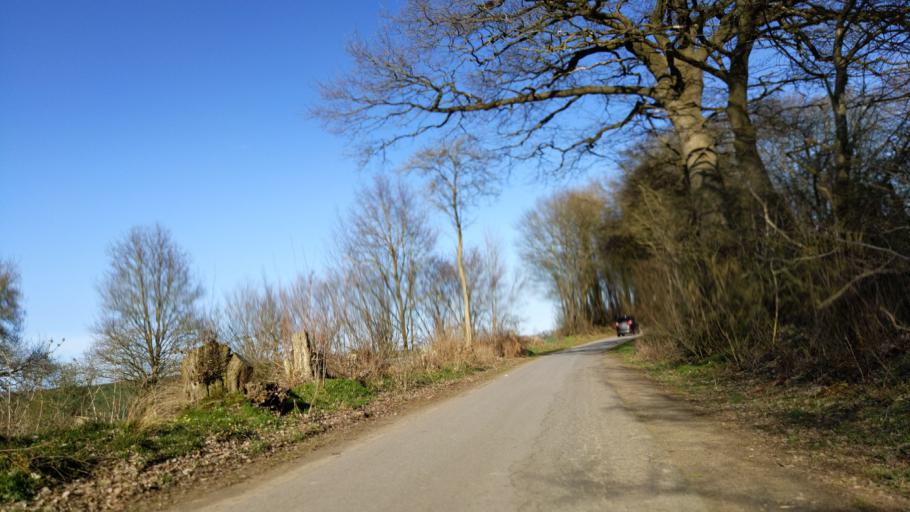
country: DE
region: Schleswig-Holstein
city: Susel
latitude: 54.0690
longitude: 10.6963
